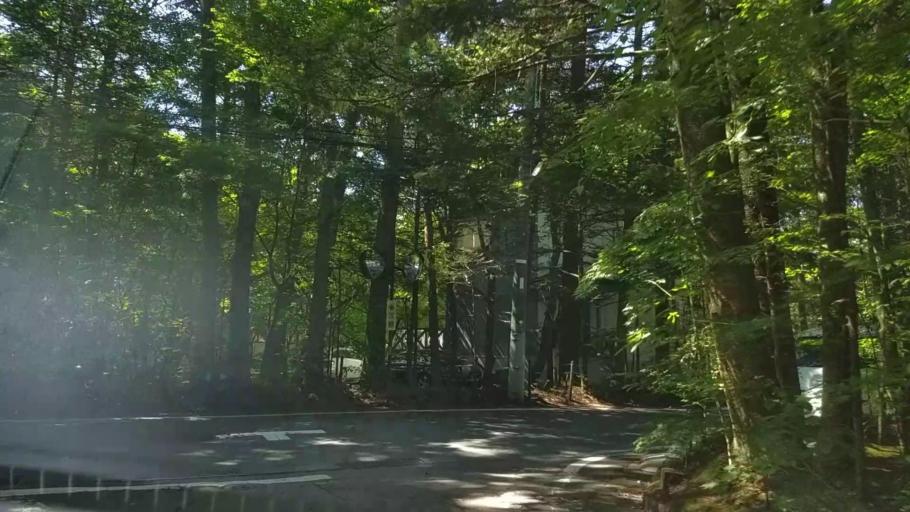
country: JP
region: Nagano
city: Saku
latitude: 36.3495
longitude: 138.6310
